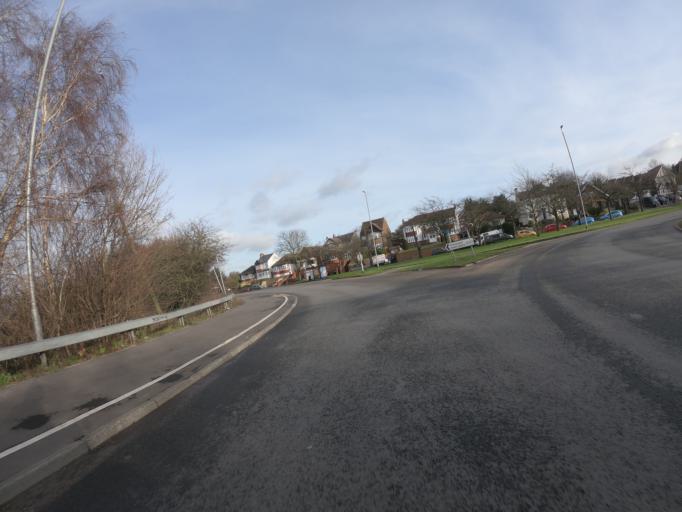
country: GB
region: England
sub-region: Kent
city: Gravesend
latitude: 51.4191
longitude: 0.3597
